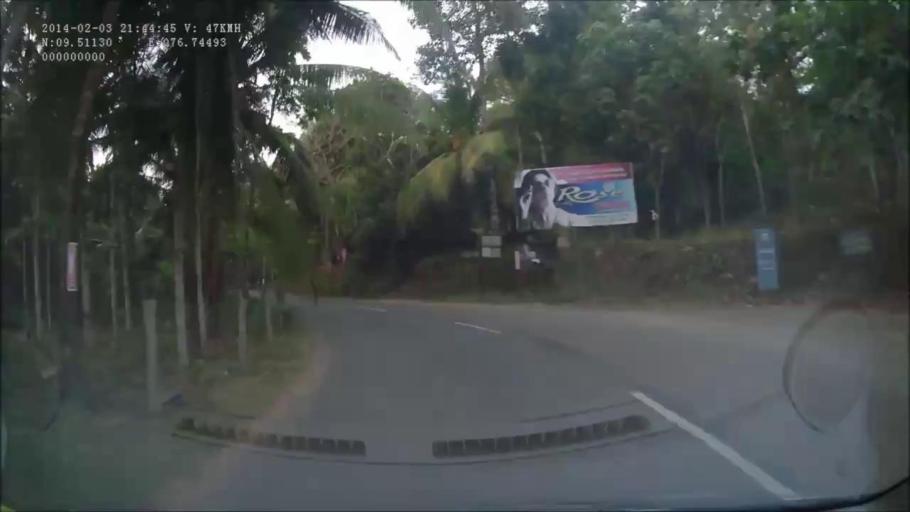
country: IN
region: Kerala
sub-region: Kottayam
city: Erattupetta
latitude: 9.5126
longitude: 76.7443
